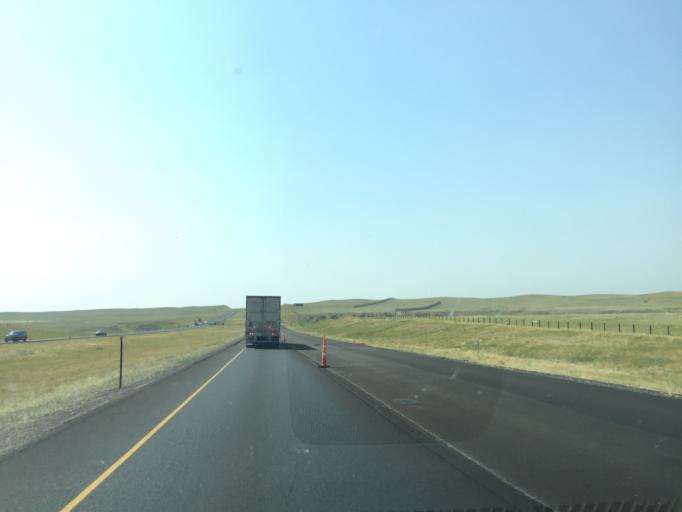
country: US
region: Wyoming
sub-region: Laramie County
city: Ranchettes
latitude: 41.3286
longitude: -104.8633
